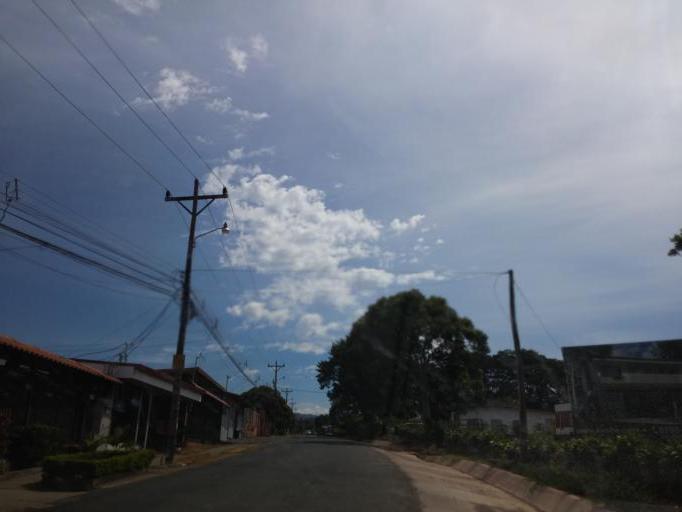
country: CR
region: Alajuela
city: Alajuela
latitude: 10.0429
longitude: -84.2337
